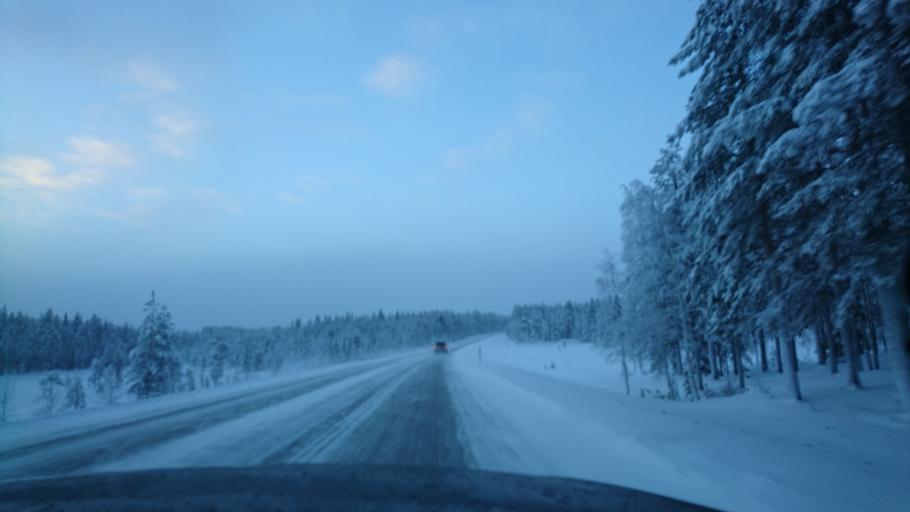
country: FI
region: Northern Ostrobothnia
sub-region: Koillismaa
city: Taivalkoski
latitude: 65.4778
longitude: 27.7896
